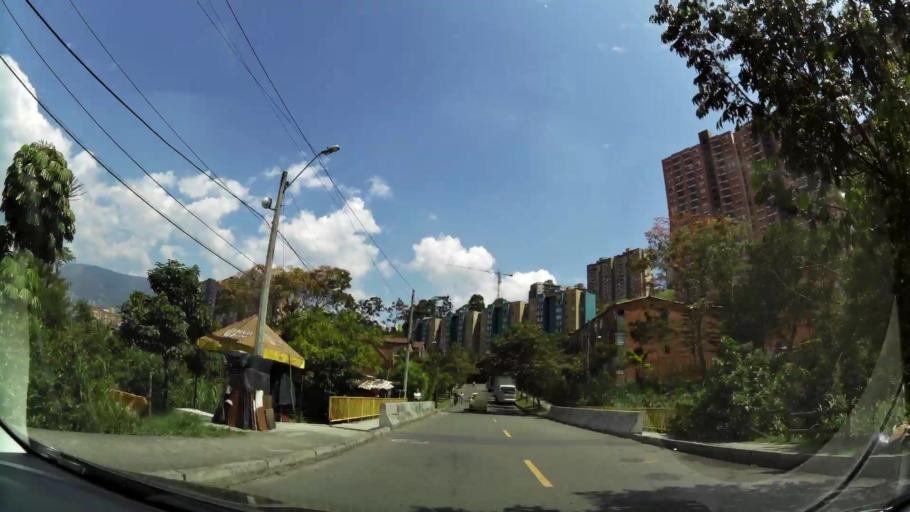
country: CO
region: Antioquia
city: Itagui
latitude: 6.2037
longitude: -75.6017
